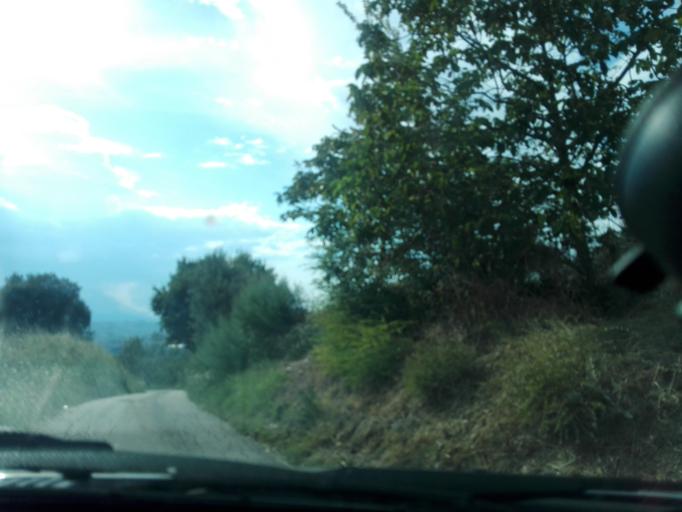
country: IT
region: Abruzzo
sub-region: Provincia di Pescara
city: Cappelle sul Tavo
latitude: 42.4573
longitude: 14.1013
